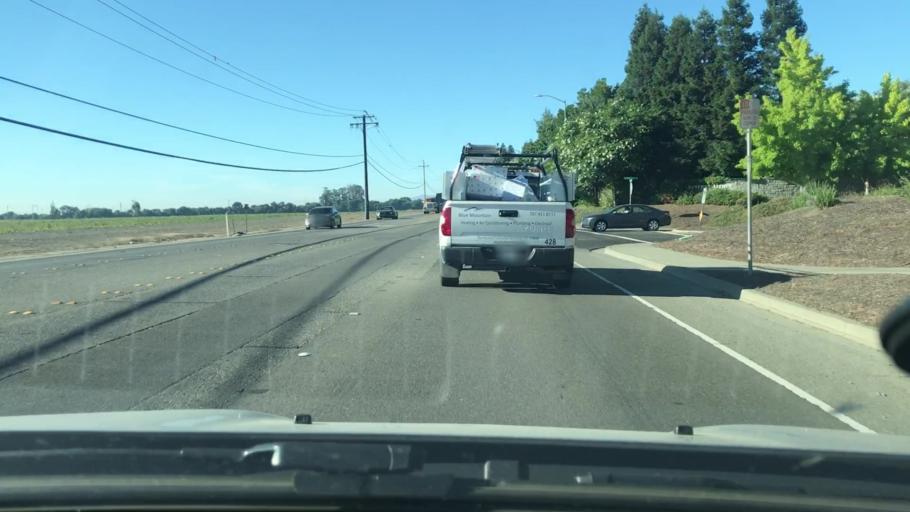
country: US
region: California
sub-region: Solano County
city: Hartley
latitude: 38.3646
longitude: -121.9341
